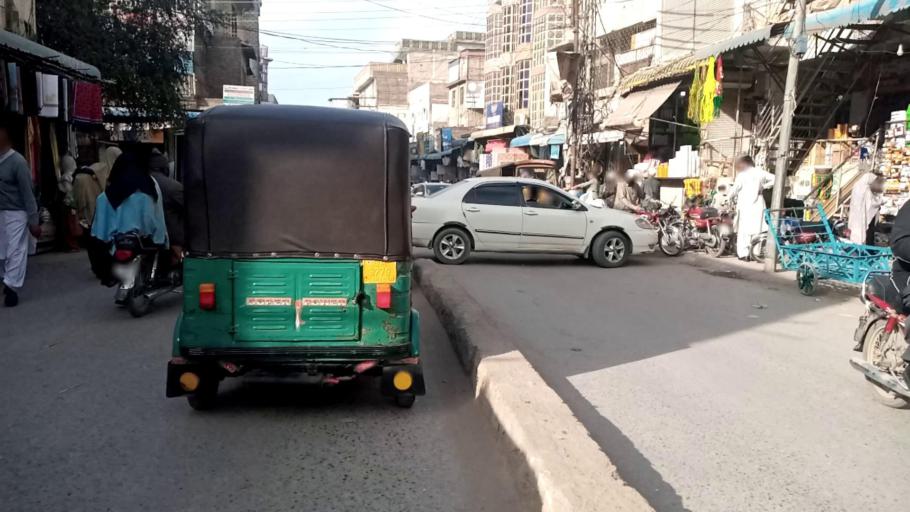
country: PK
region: Khyber Pakhtunkhwa
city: Peshawar
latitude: 34.0108
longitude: 71.5746
